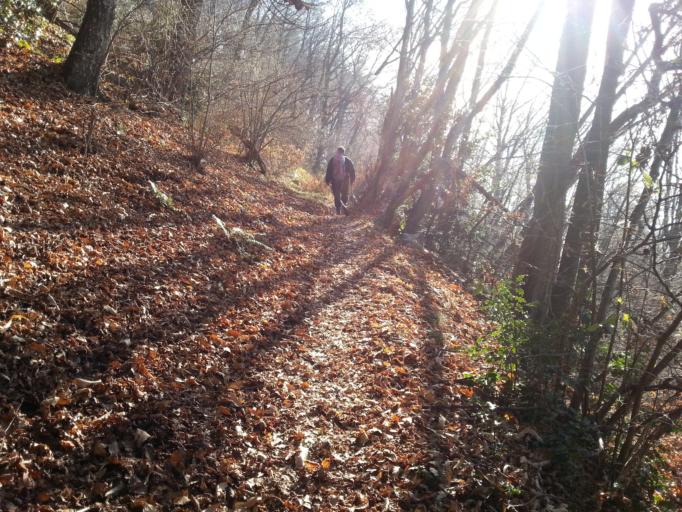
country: IT
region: Lombardy
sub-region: Provincia di Como
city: Maslianico
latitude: 45.8615
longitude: 9.0462
